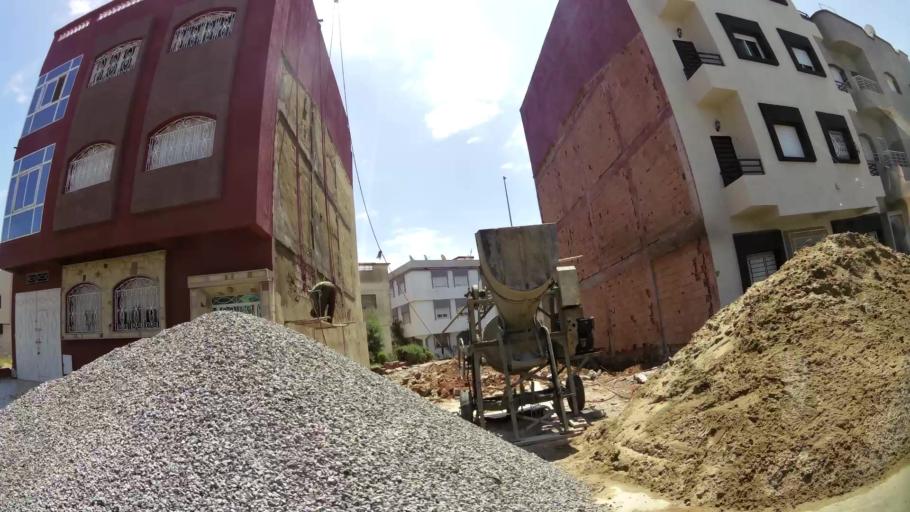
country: MA
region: Gharb-Chrarda-Beni Hssen
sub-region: Kenitra Province
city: Kenitra
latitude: 34.2710
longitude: -6.6126
